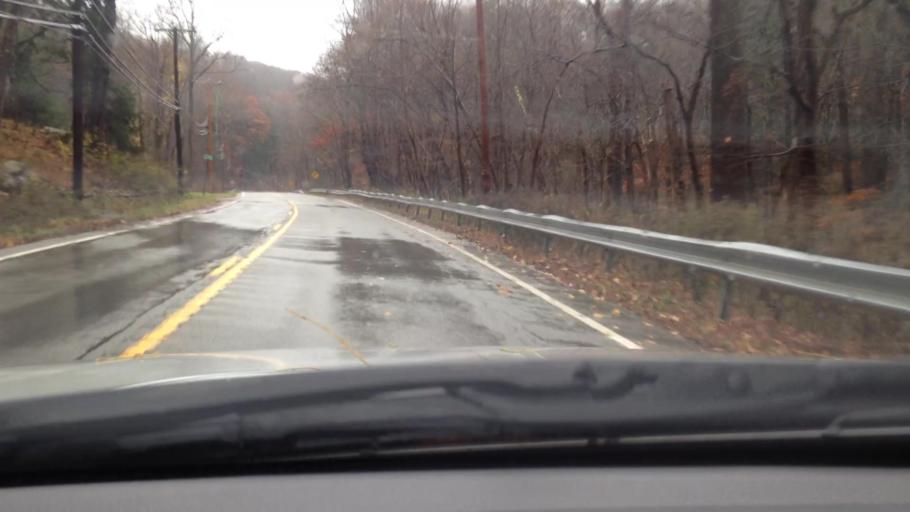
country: US
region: New York
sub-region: Orange County
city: Highland Falls
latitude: 41.3648
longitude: -73.9274
